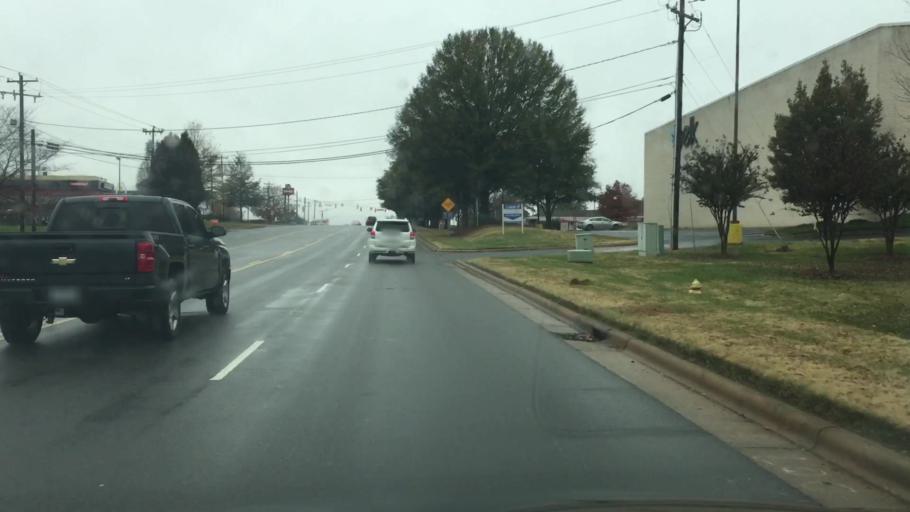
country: US
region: North Carolina
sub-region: Iredell County
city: Mooresville
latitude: 35.5932
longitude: -80.8536
